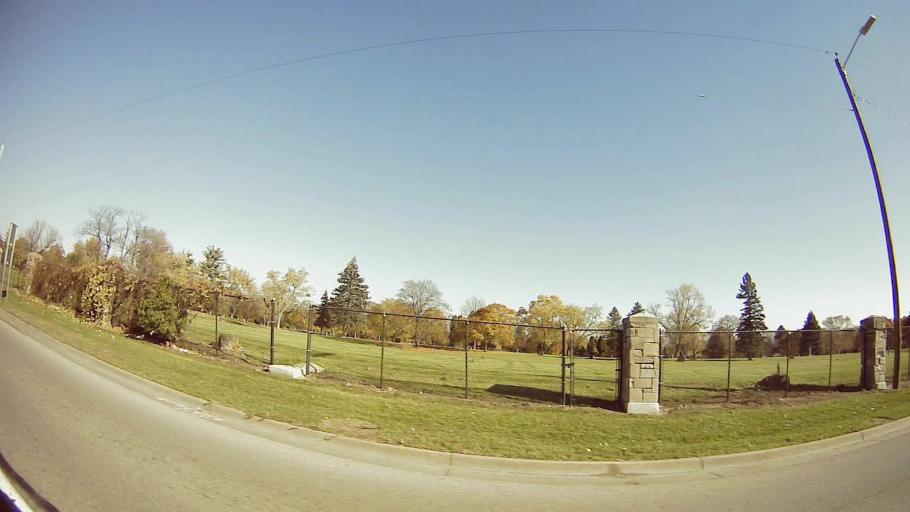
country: US
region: Michigan
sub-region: Wayne County
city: Redford
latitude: 42.4164
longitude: -83.2769
